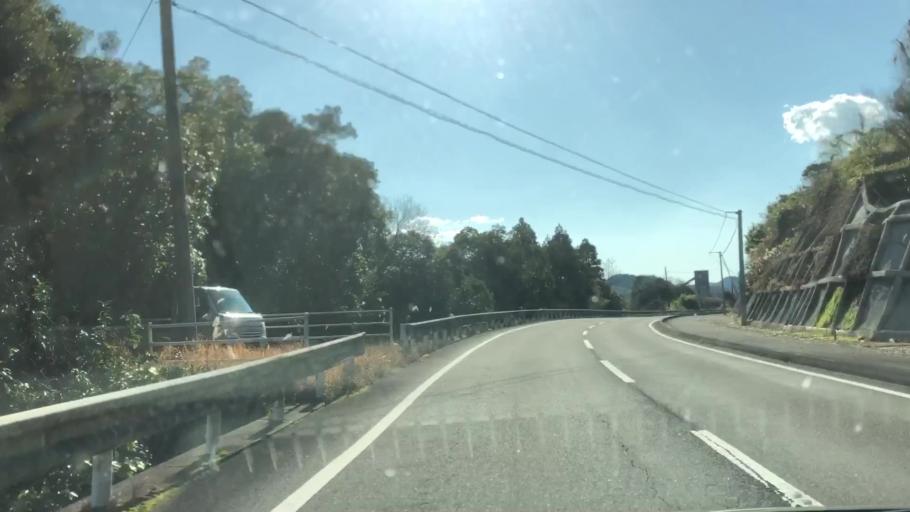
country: JP
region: Kagoshima
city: Satsumasendai
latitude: 31.8636
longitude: 130.4188
